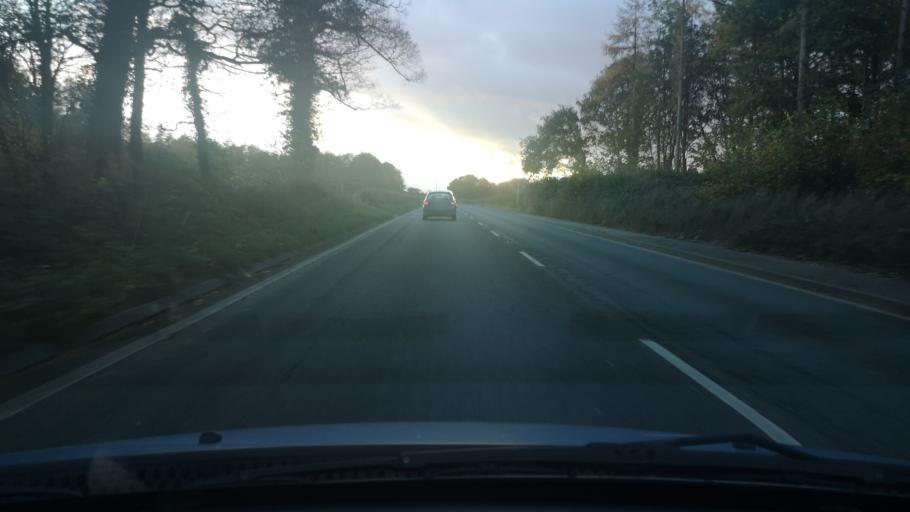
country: GB
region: England
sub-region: City and Borough of Wakefield
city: Horbury
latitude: 53.6318
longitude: -1.5619
